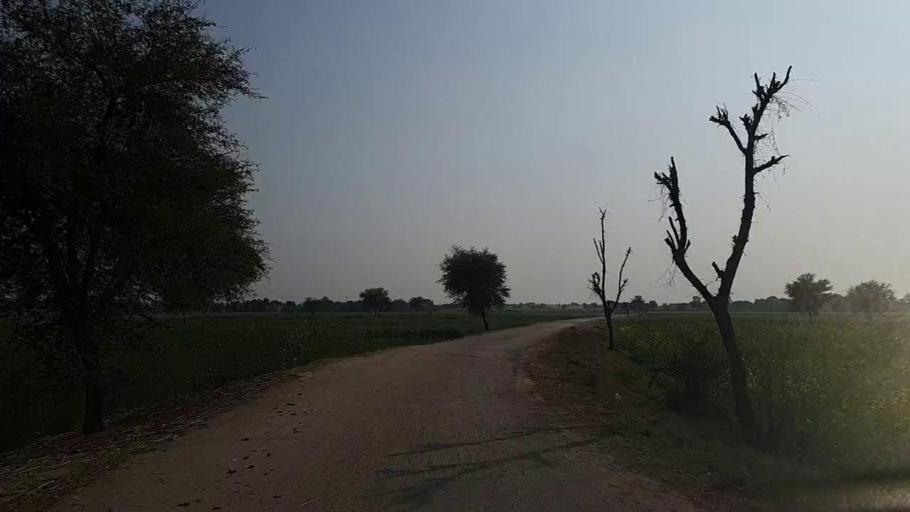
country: PK
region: Sindh
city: Daur
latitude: 26.4041
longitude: 68.4176
